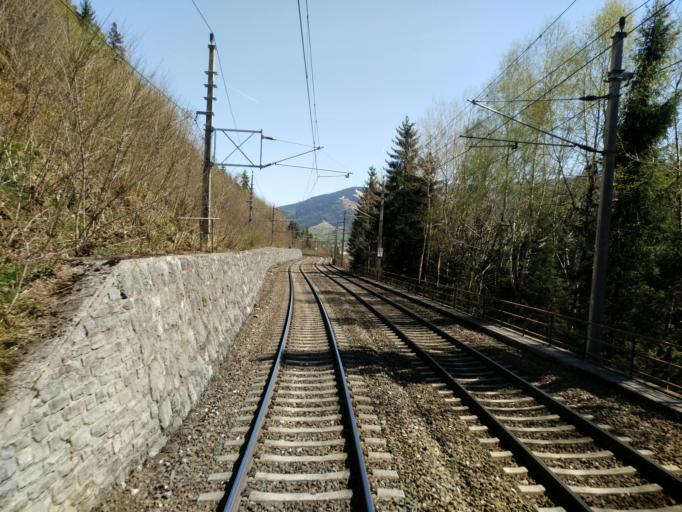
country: AT
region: Salzburg
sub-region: Politischer Bezirk Zell am See
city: Leogang
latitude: 47.4433
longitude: 12.7087
